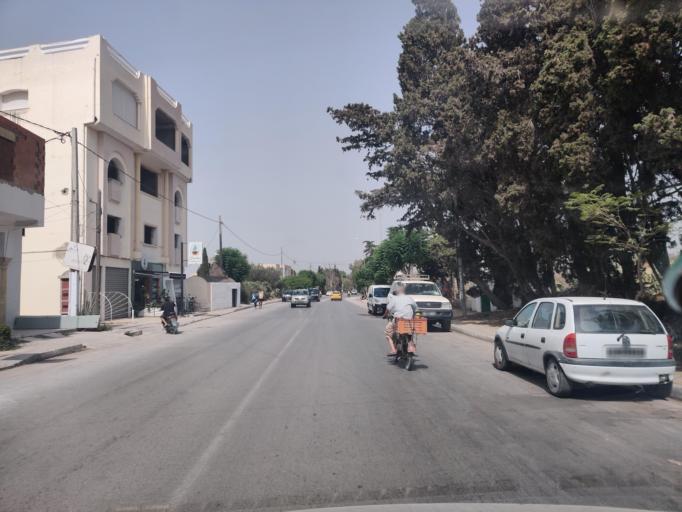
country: TN
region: Nabul
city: Al Hammamat
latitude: 36.4093
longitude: 10.6040
